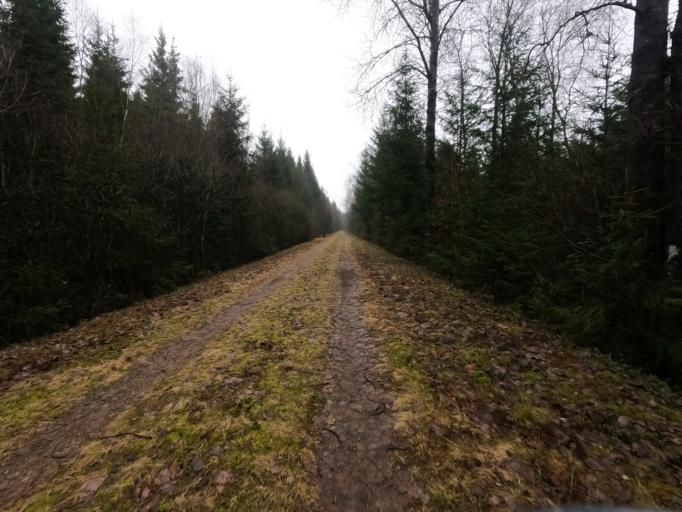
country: SE
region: Halland
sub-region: Hylte Kommun
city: Hyltebruk
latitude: 56.8124
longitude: 13.2773
